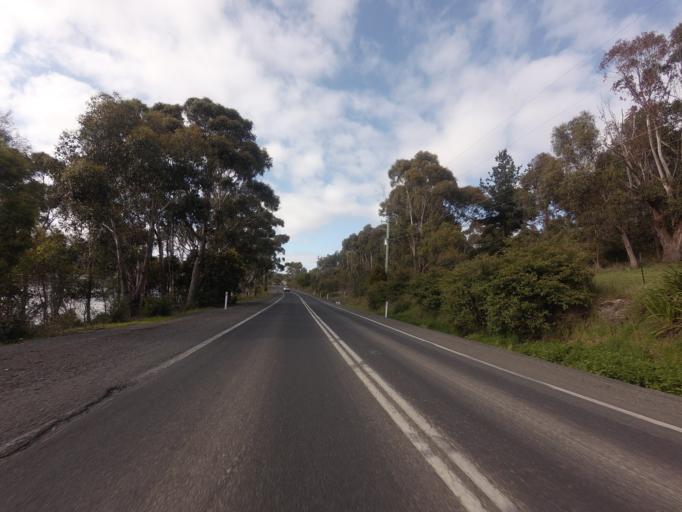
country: AU
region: Tasmania
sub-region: Huon Valley
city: Geeveston
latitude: -43.1502
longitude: 146.9801
